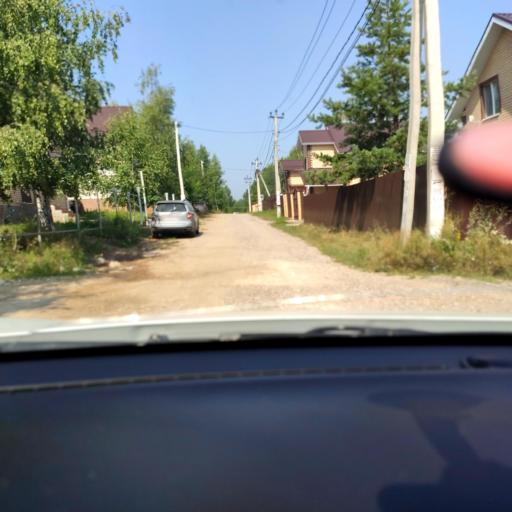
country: RU
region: Tatarstan
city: Stolbishchi
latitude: 55.7379
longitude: 49.2548
